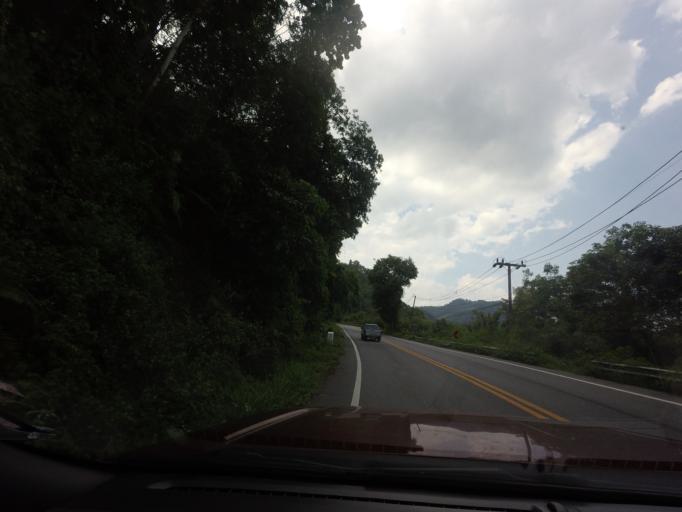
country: TH
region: Yala
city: Than To
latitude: 6.0392
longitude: 101.1975
